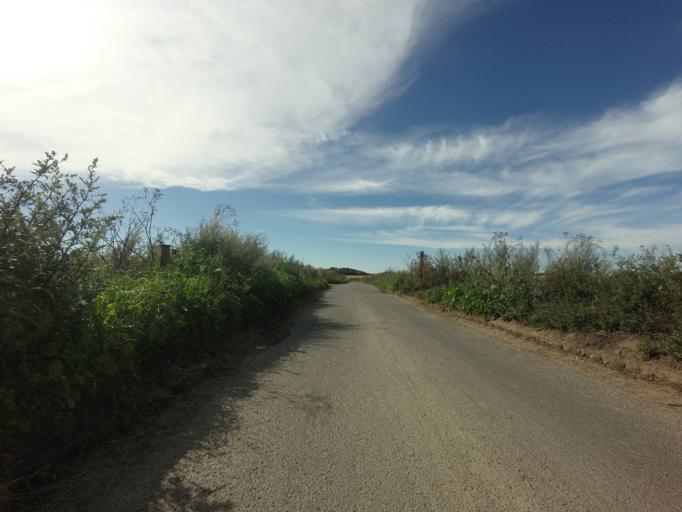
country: GB
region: England
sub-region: Kent
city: Herne Bay
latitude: 51.3666
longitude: 1.1932
